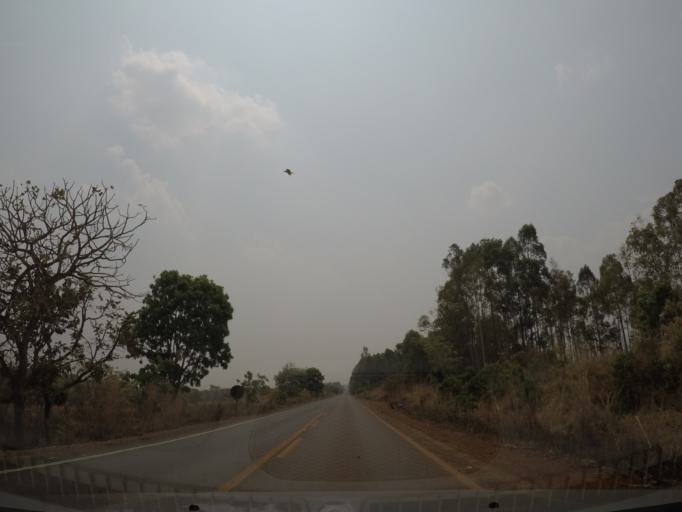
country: BR
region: Goias
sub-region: Pirenopolis
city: Pirenopolis
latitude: -15.9157
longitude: -48.8580
